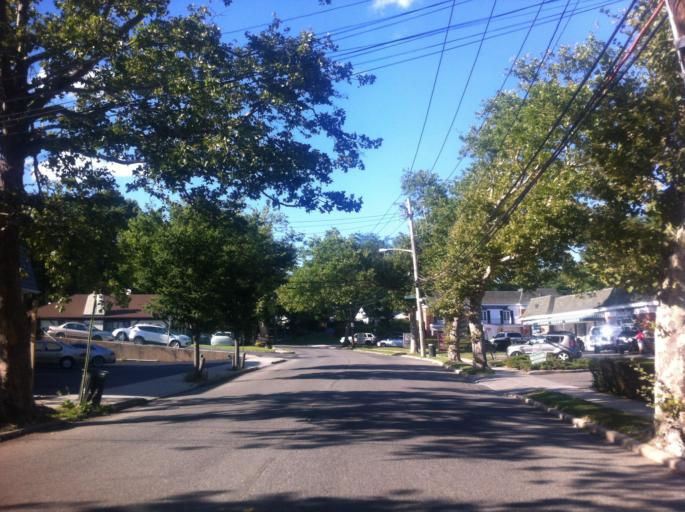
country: US
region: New York
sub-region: Nassau County
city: Locust Valley
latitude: 40.8788
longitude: -73.5966
